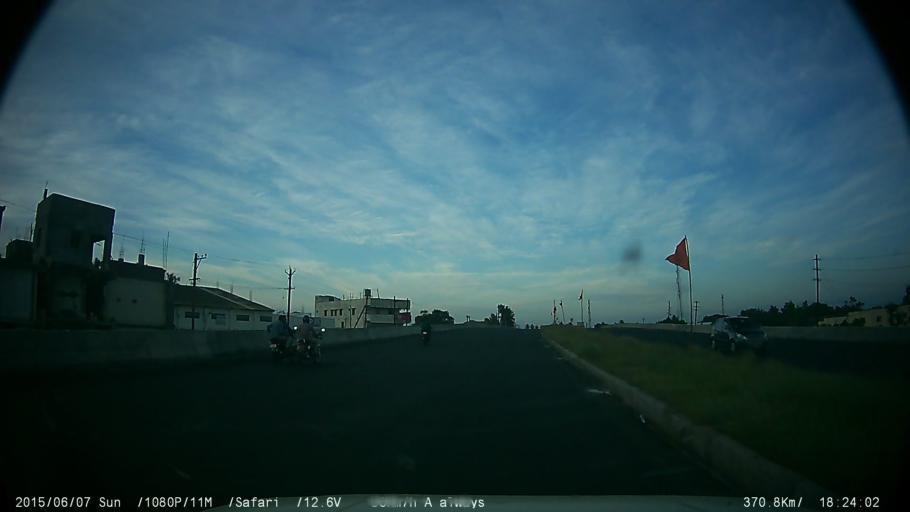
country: IN
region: Tamil Nadu
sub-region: Coimbatore
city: Sulur
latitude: 11.1034
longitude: 77.1693
